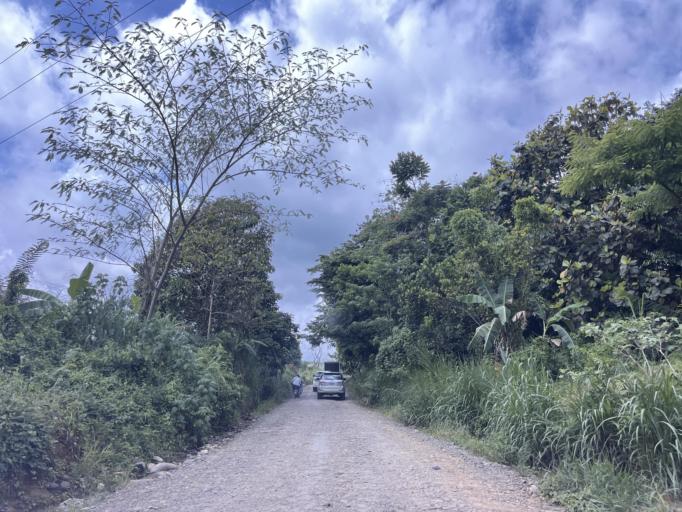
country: PH
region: Northern Mindanao
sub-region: Province of Bukidnon
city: Impalutao
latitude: 8.2551
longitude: 125.0042
